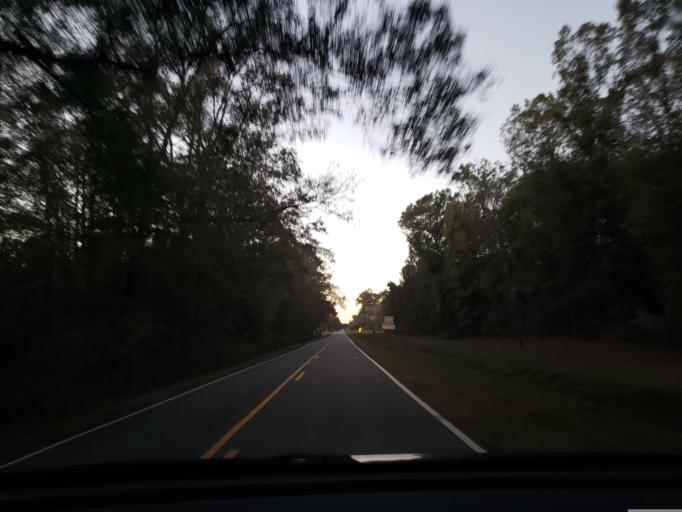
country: US
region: North Carolina
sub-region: Duplin County
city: Beulaville
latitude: 34.7674
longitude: -77.7356
